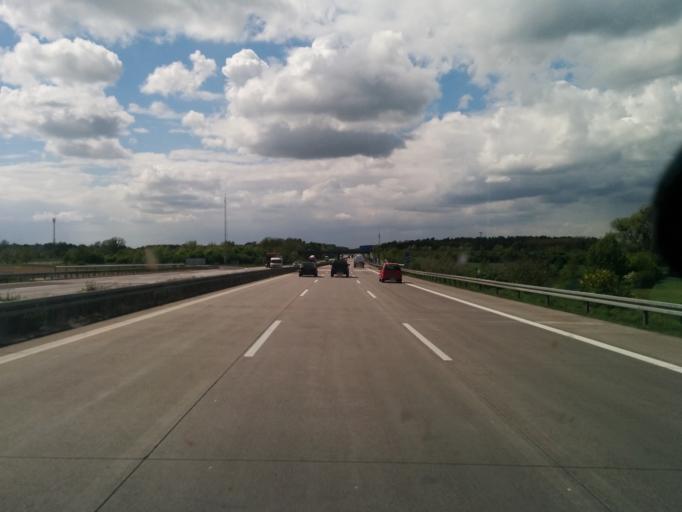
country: DE
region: Saxony-Anhalt
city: Schermen
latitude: 52.2256
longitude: 11.8277
